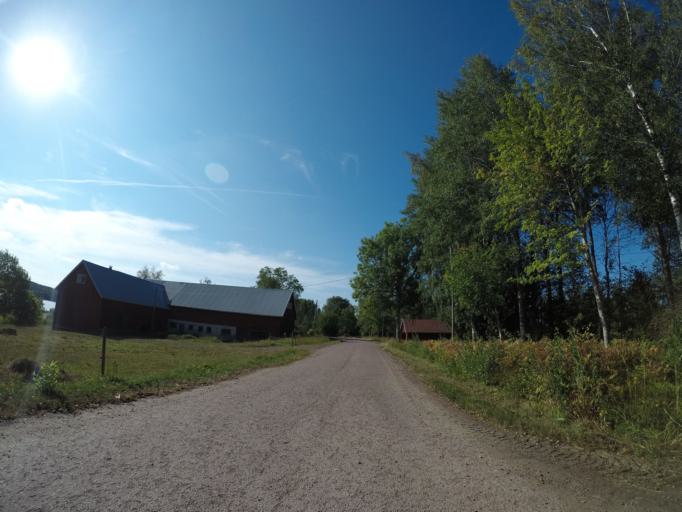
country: AX
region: Alands landsbygd
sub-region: Finstroem
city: Finstroem
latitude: 60.2472
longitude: 19.9217
